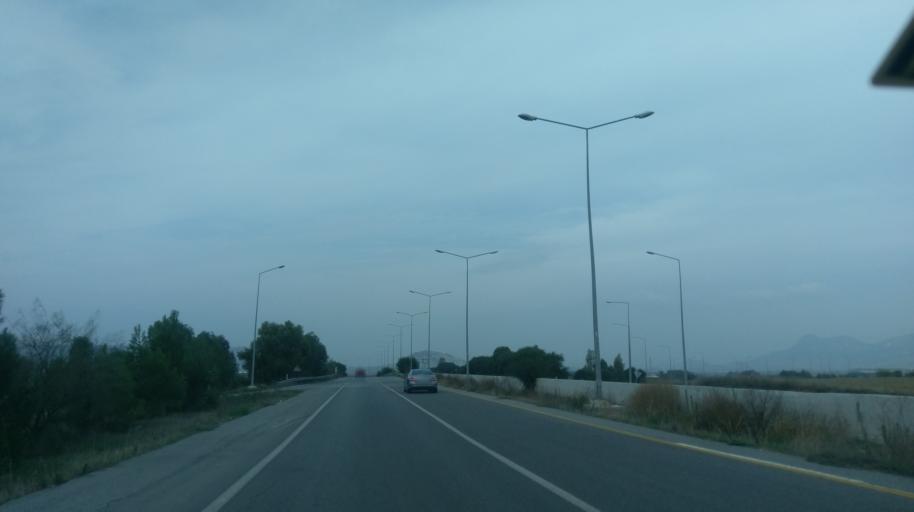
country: CY
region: Lefkosia
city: Mammari
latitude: 35.2164
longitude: 33.1808
